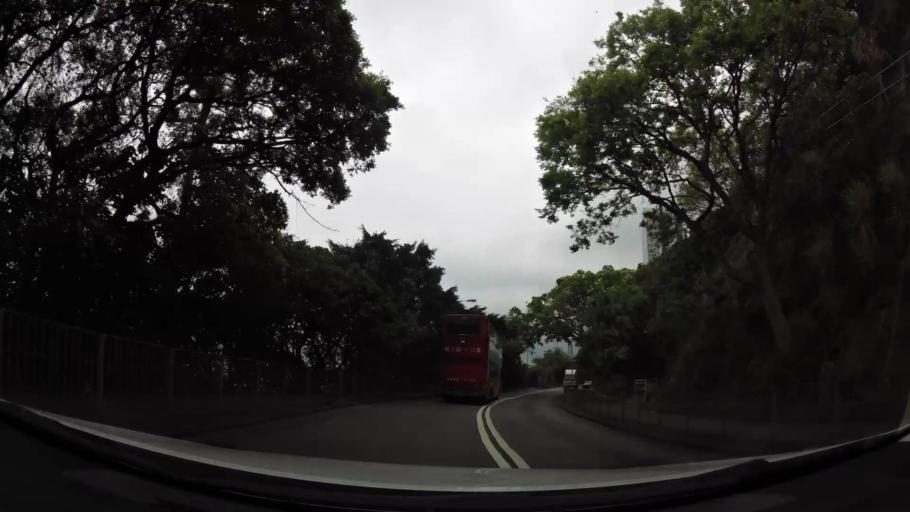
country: HK
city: Hong Kong
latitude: 22.2799
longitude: 114.1181
